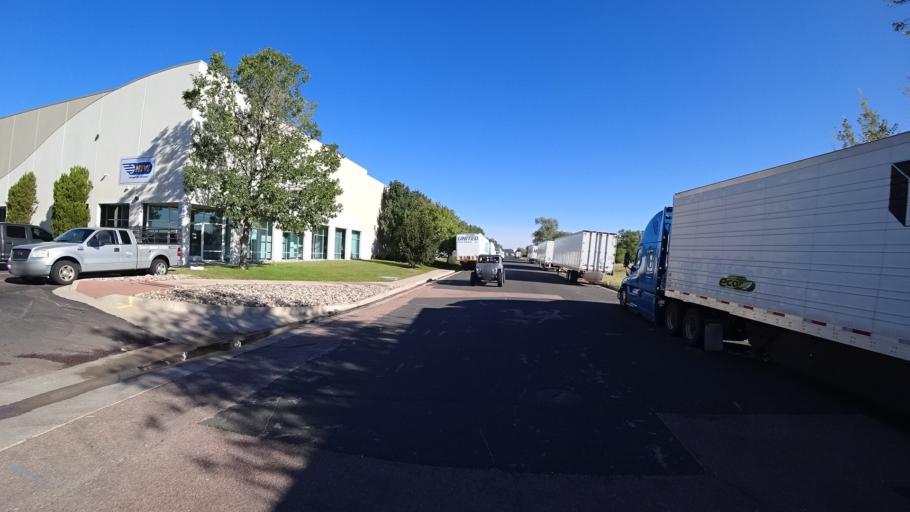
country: US
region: Colorado
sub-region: El Paso County
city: Cimarron Hills
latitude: 38.8089
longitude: -104.7284
